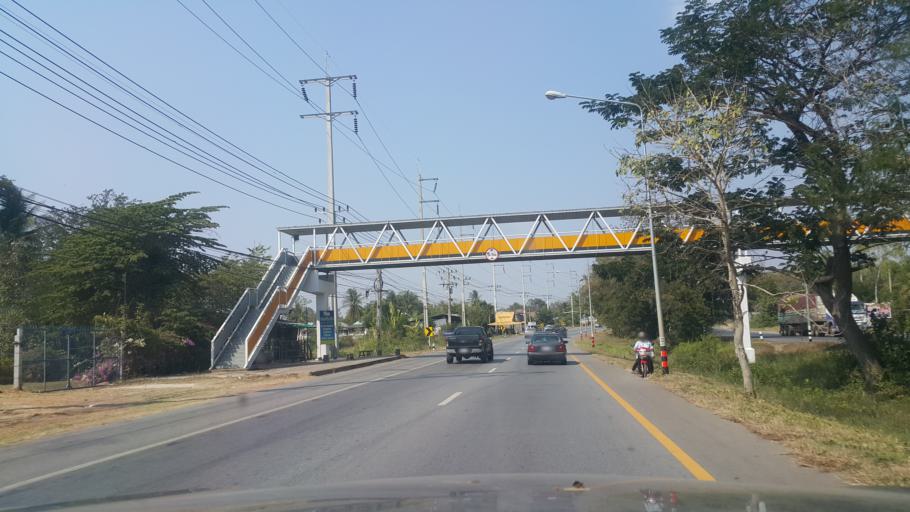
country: TH
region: Nakhon Ratchasima
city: Pak Thong Chai
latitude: 14.6179
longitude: 102.0066
